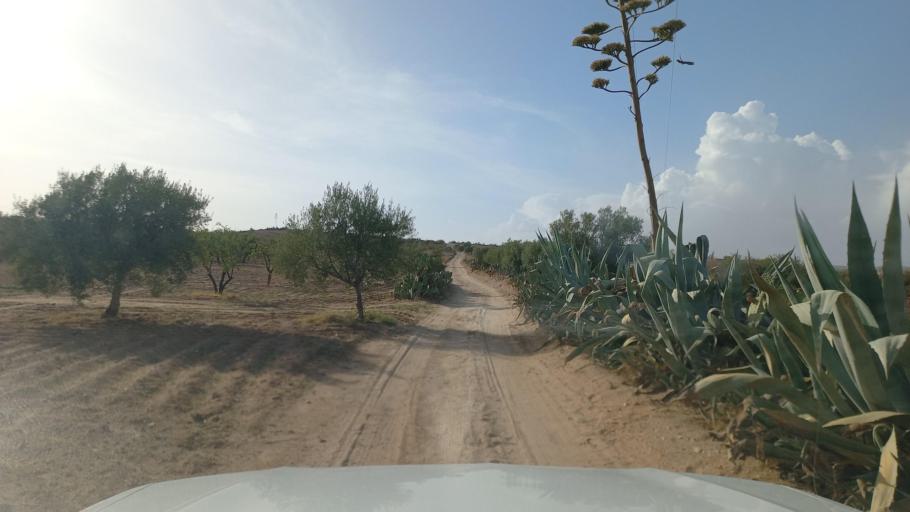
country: TN
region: Al Qasrayn
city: Kasserine
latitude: 35.2331
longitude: 8.9206
